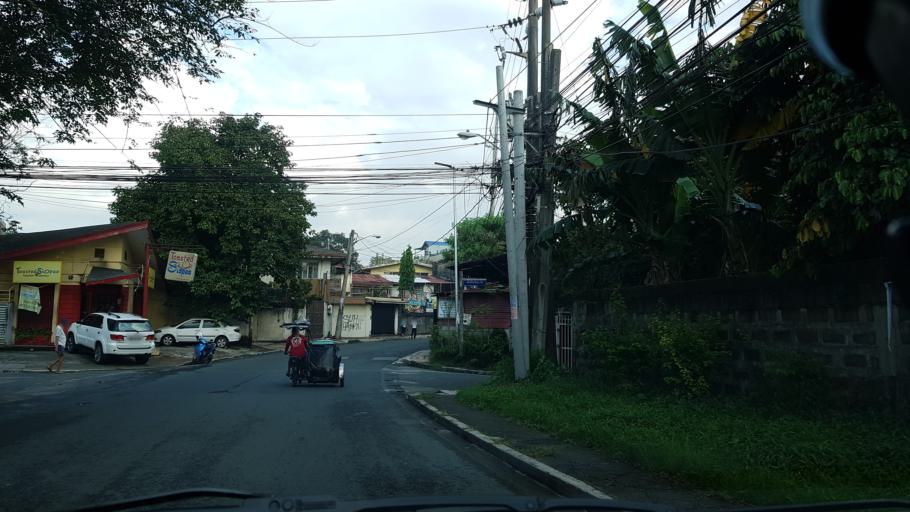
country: PH
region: Metro Manila
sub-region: Quezon City
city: Quezon City
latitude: 14.6394
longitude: 121.0573
